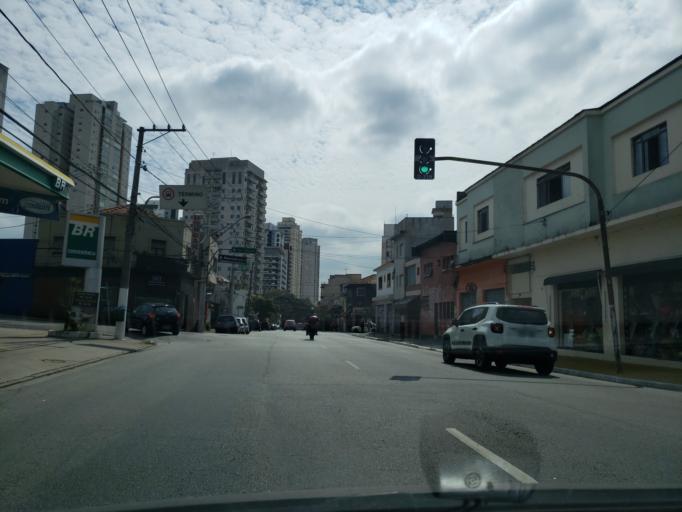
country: BR
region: Sao Paulo
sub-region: Sao Paulo
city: Sao Paulo
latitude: -23.5979
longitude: -46.6055
